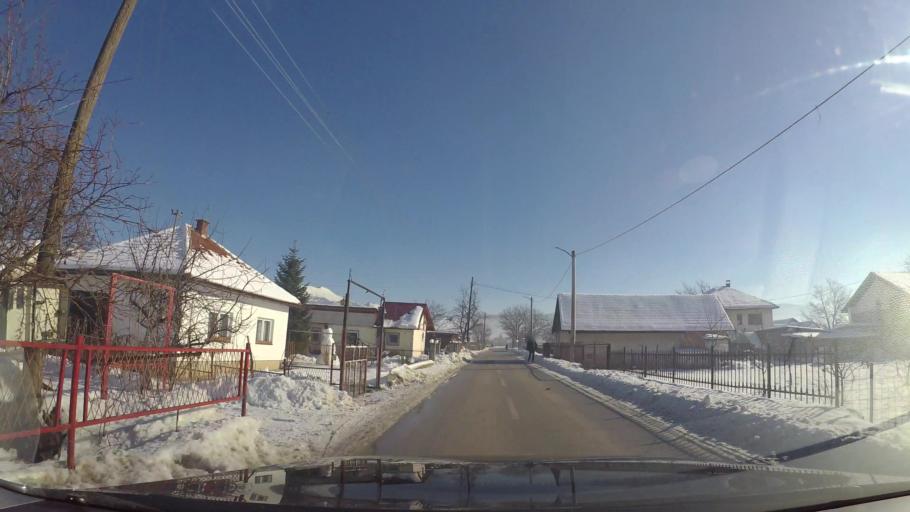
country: BA
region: Federation of Bosnia and Herzegovina
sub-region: Kanton Sarajevo
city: Sarajevo
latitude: 43.7968
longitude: 18.3427
